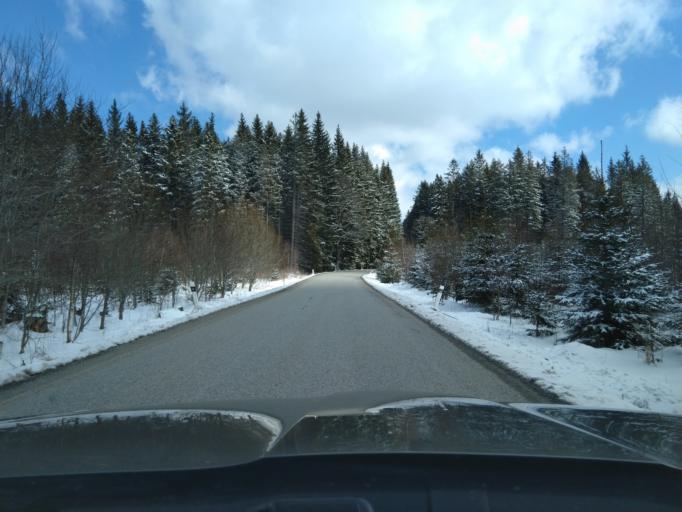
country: CZ
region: Jihocesky
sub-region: Okres Prachatice
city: Zdikov
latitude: 49.0462
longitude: 13.6812
